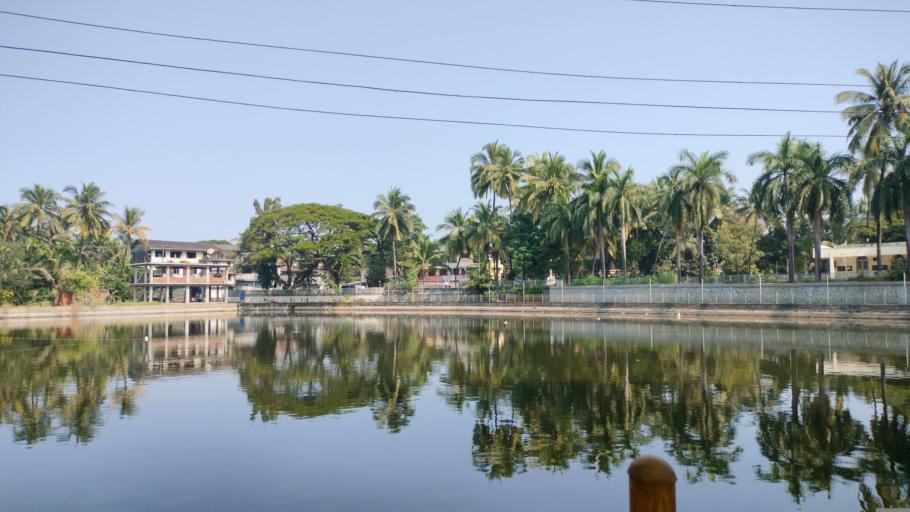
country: IN
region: Maharashtra
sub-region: Thane
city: Virar
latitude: 19.4390
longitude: 72.7824
